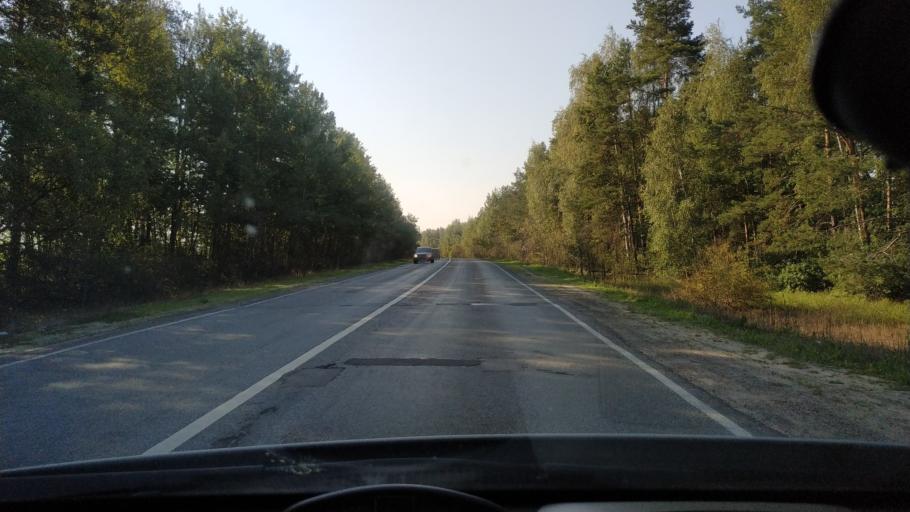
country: RU
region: Moskovskaya
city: Tugolesskiy Bor
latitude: 55.5402
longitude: 39.7051
